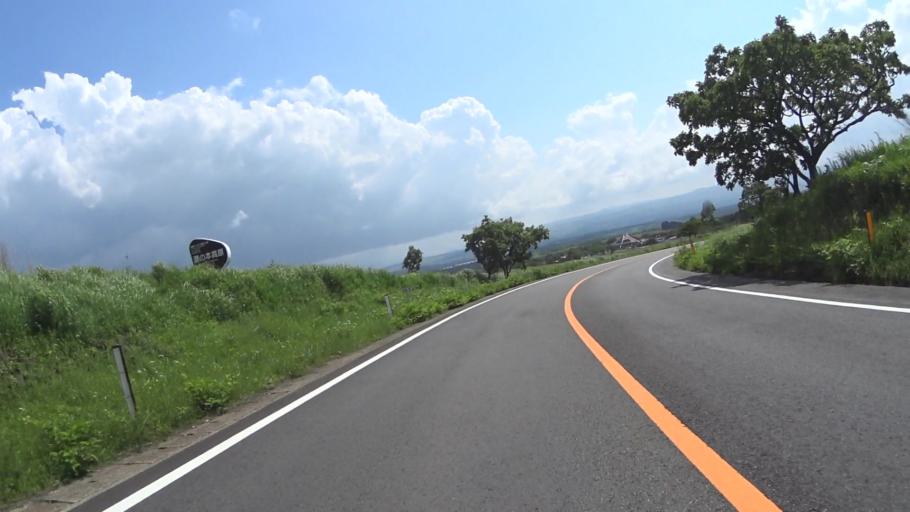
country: JP
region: Kumamoto
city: Aso
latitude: 33.0742
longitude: 131.1949
